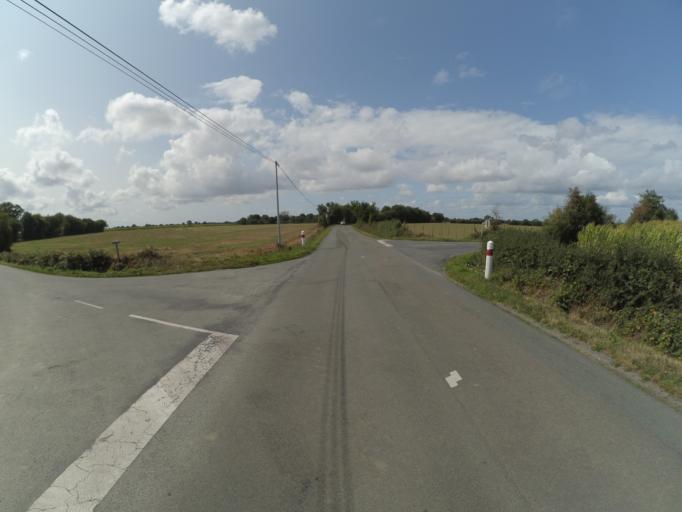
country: FR
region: Pays de la Loire
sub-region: Departement de la Vendee
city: La Bruffiere
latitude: 47.0191
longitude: -1.2183
